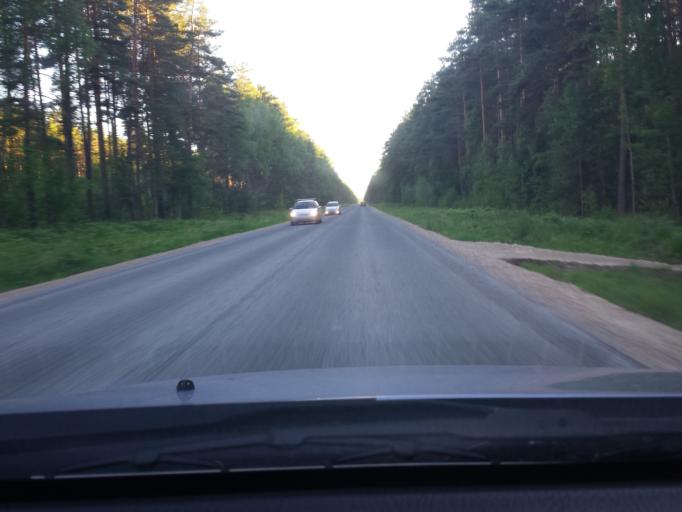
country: LV
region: Carnikava
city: Carnikava
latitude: 57.1115
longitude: 24.2345
